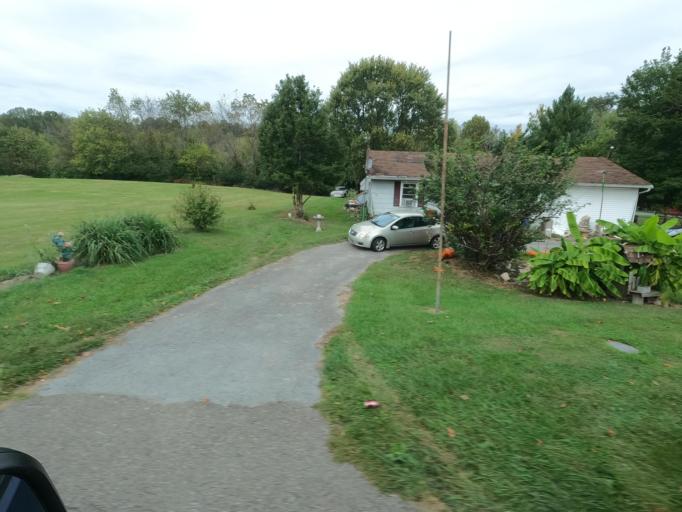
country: US
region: Tennessee
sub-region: Washington County
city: Jonesborough
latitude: 36.2446
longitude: -82.5541
